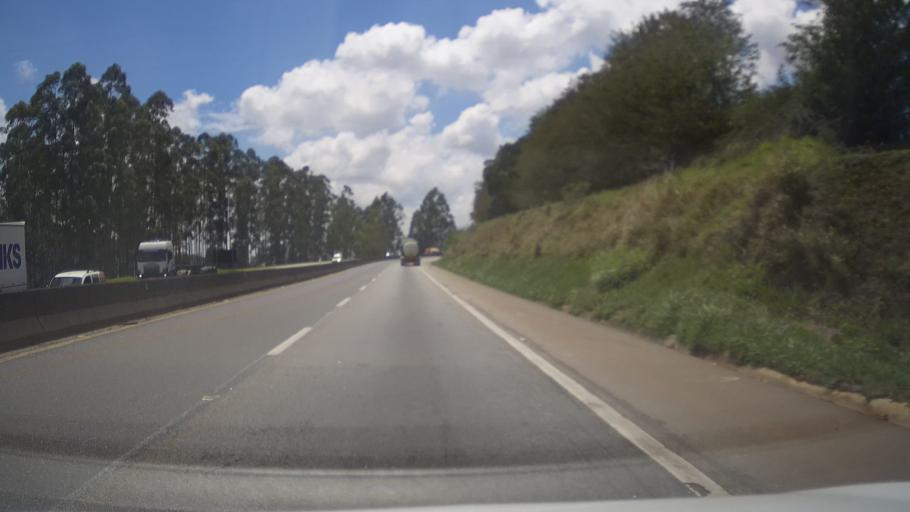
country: BR
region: Minas Gerais
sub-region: Campanha
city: Campanha
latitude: -21.8073
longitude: -45.4799
